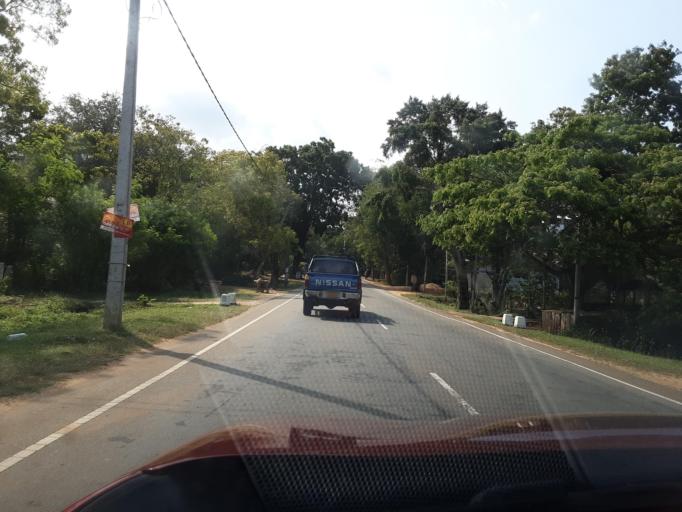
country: LK
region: Uva
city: Haputale
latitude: 6.3549
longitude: 81.1916
